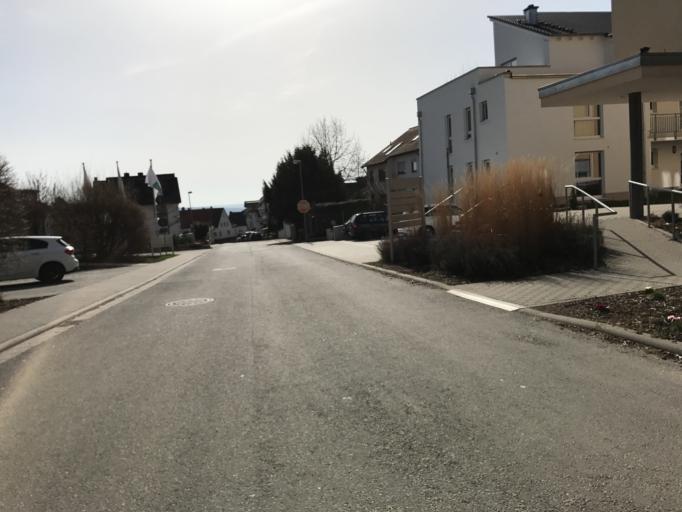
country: DE
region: Rheinland-Pfalz
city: Essenheim
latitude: 49.9329
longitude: 8.1531
